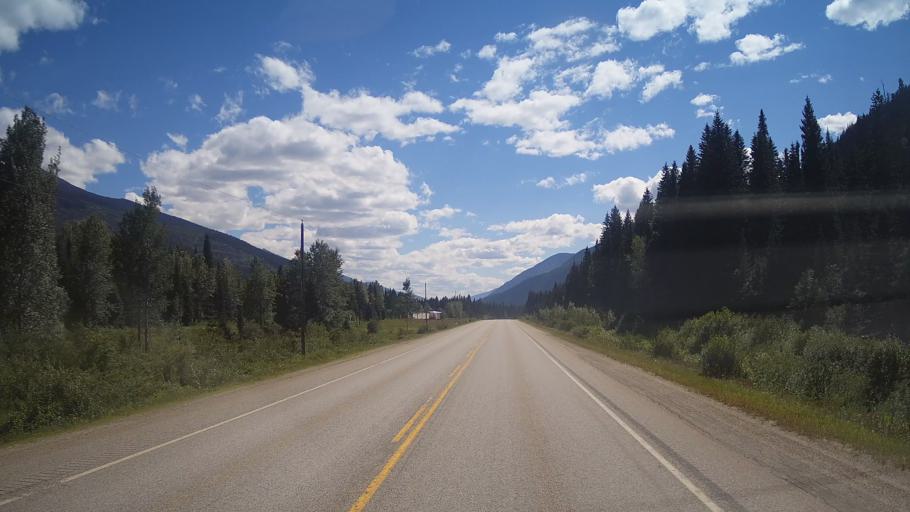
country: CA
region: Alberta
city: Jasper Park Lodge
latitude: 52.5785
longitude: -119.0968
